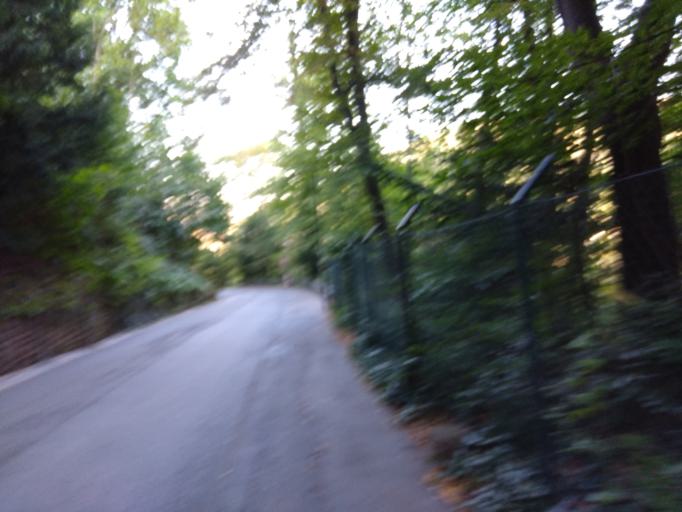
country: DE
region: Baden-Wuerttemberg
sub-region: Karlsruhe Region
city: Heidelberg
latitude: 49.4092
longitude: 8.7183
